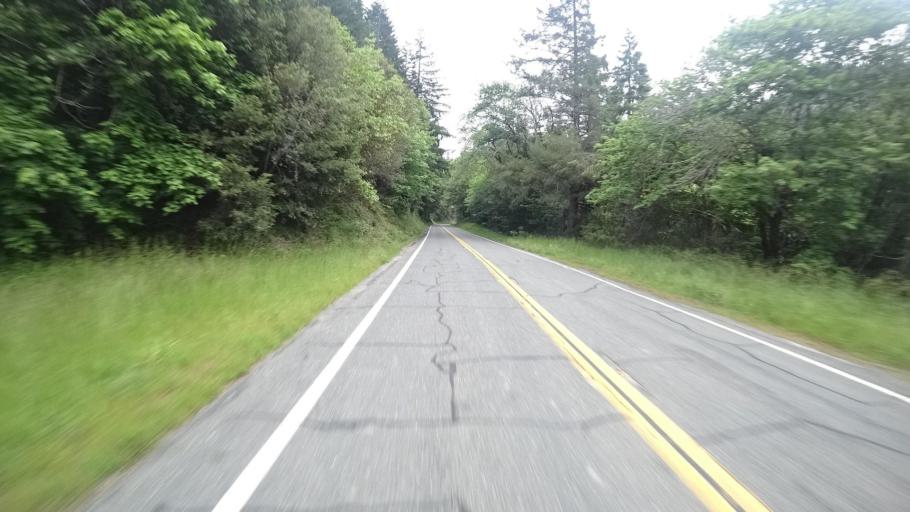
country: US
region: California
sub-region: Humboldt County
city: Willow Creek
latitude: 41.2067
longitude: -123.6620
